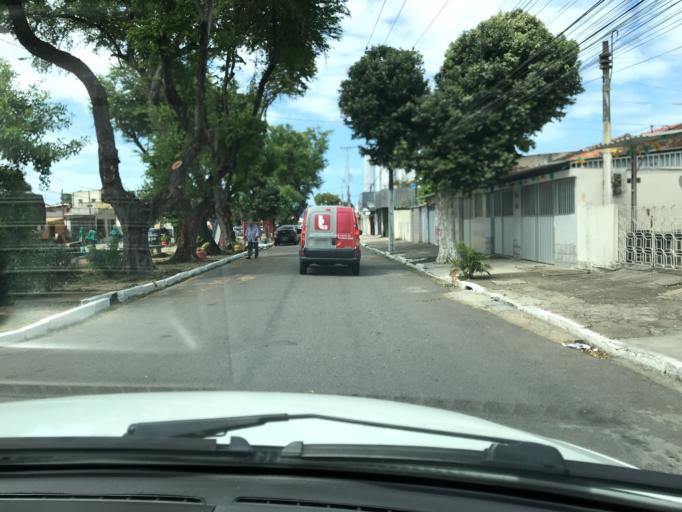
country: BR
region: Pernambuco
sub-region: Recife
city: Recife
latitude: -8.0443
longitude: -34.8836
